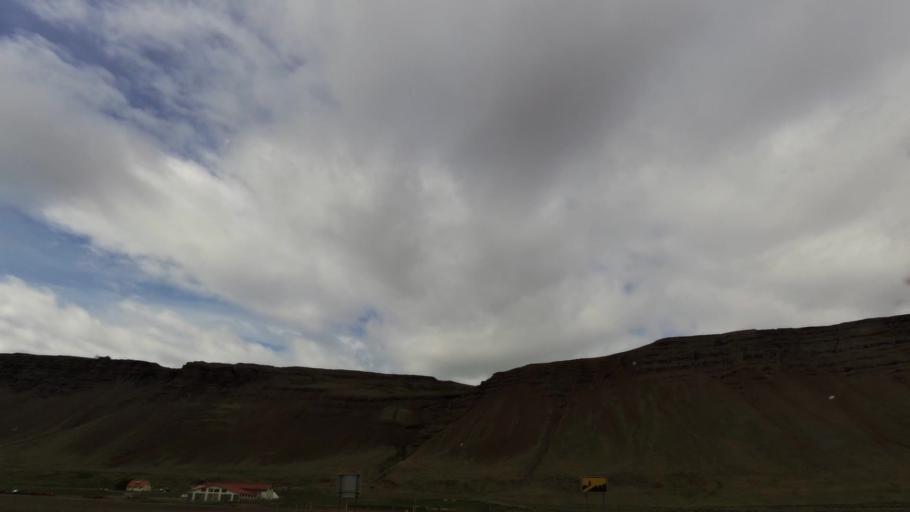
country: IS
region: West
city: Stykkisholmur
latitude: 65.4542
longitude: -22.2010
